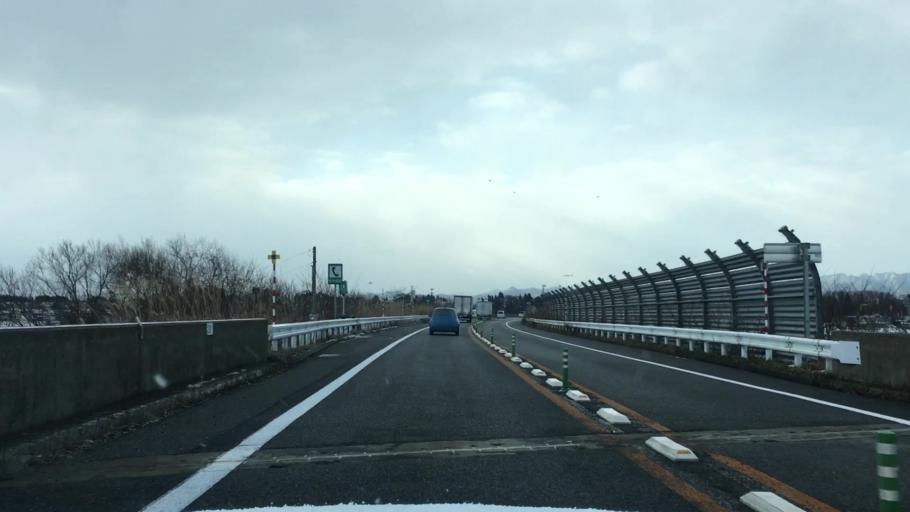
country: JP
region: Akita
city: Odate
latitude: 40.2848
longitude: 140.5409
